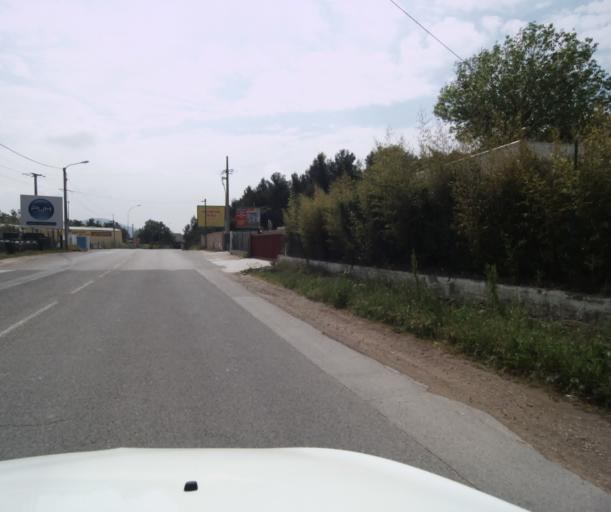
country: FR
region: Provence-Alpes-Cote d'Azur
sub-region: Departement du Var
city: La Farlede
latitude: 43.1426
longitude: 6.0290
